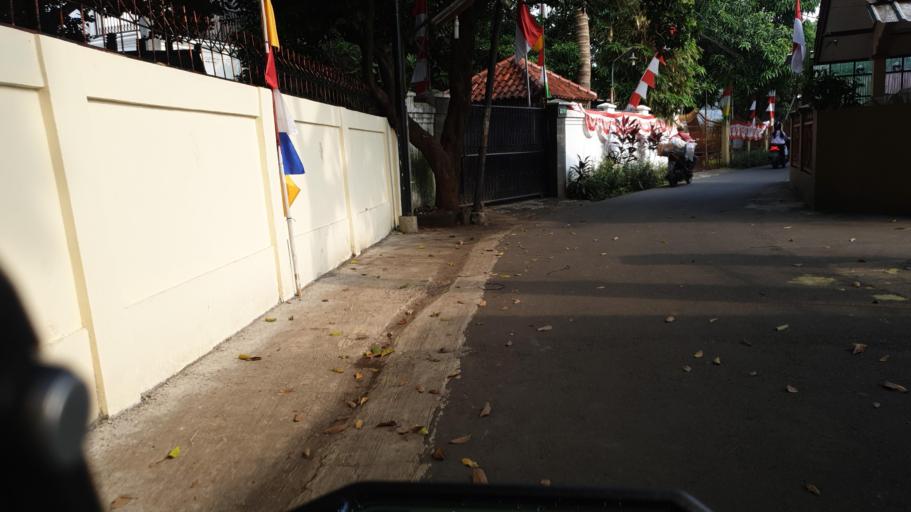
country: ID
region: West Java
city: Depok
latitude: -6.3384
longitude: 106.8309
